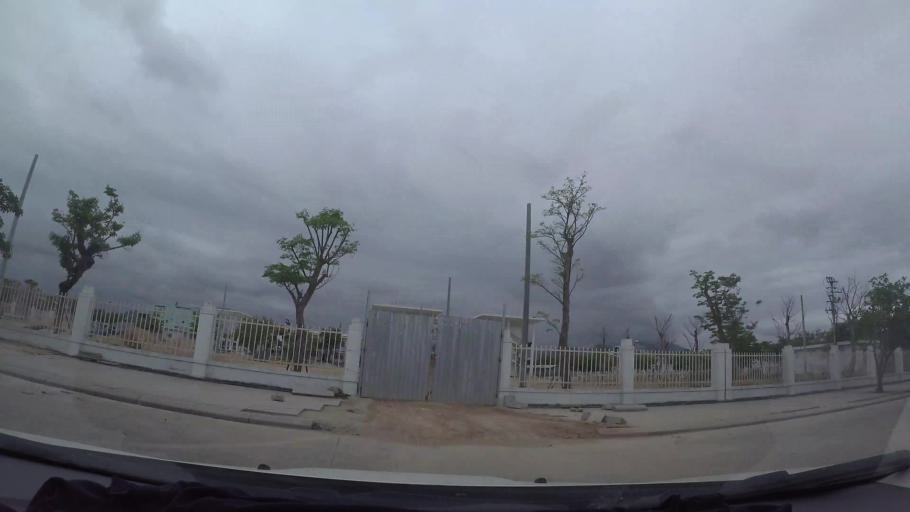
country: VN
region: Da Nang
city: Lien Chieu
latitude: 16.1034
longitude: 108.1175
